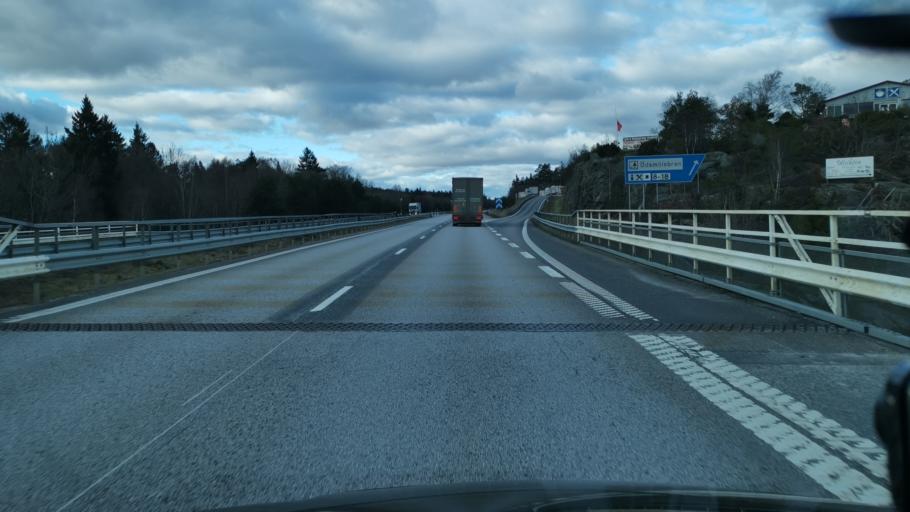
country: SE
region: Vaestra Goetaland
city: Svanesund
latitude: 58.1121
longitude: 11.8794
